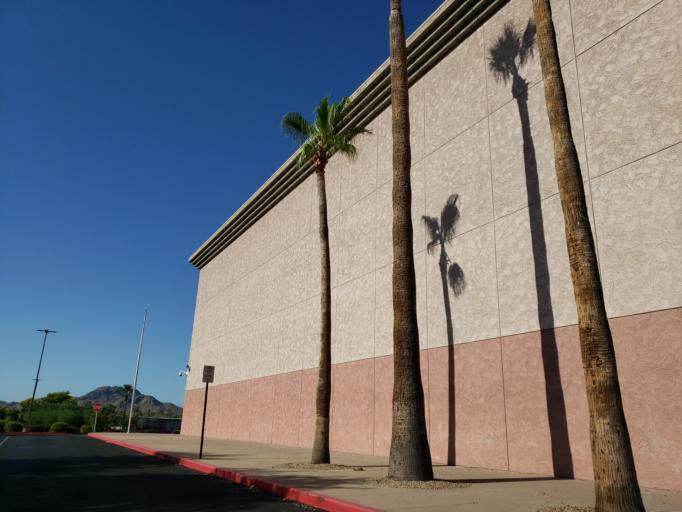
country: US
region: Arizona
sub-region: Maricopa County
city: Paradise Valley
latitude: 33.6018
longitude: -111.9811
